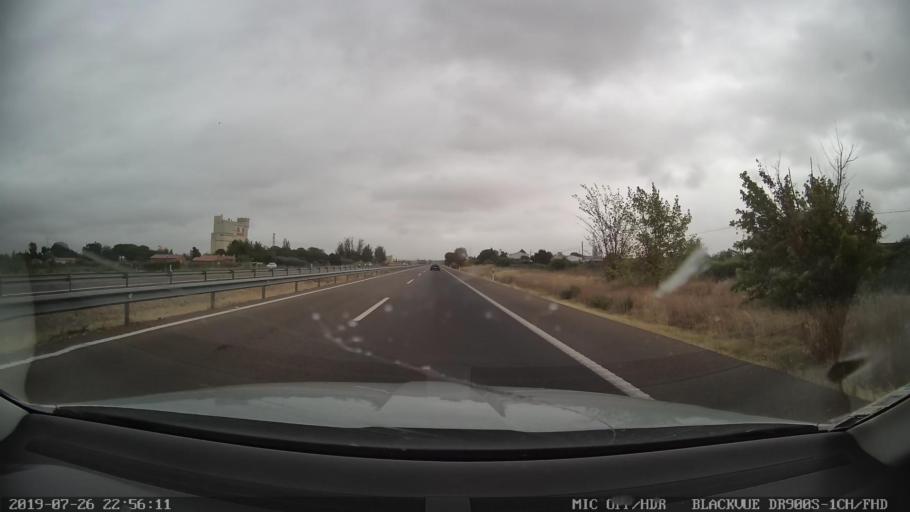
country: ES
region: Extremadura
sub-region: Provincia de Badajoz
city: Calamonte
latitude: 38.8945
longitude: -6.4211
